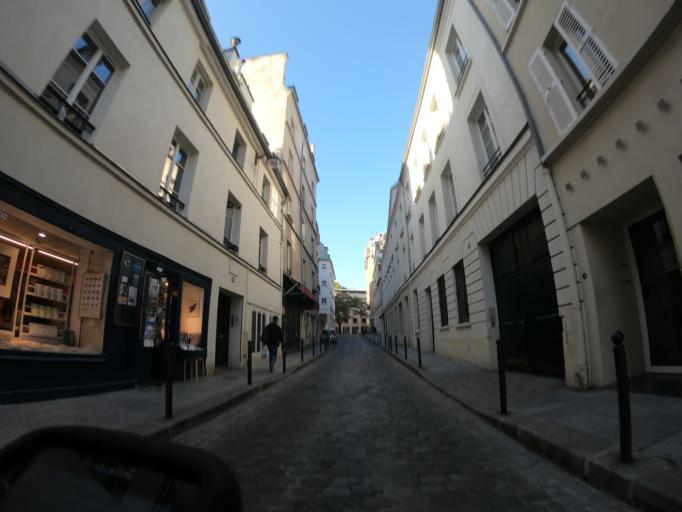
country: FR
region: Ile-de-France
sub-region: Paris
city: Paris
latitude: 48.8436
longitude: 2.3482
